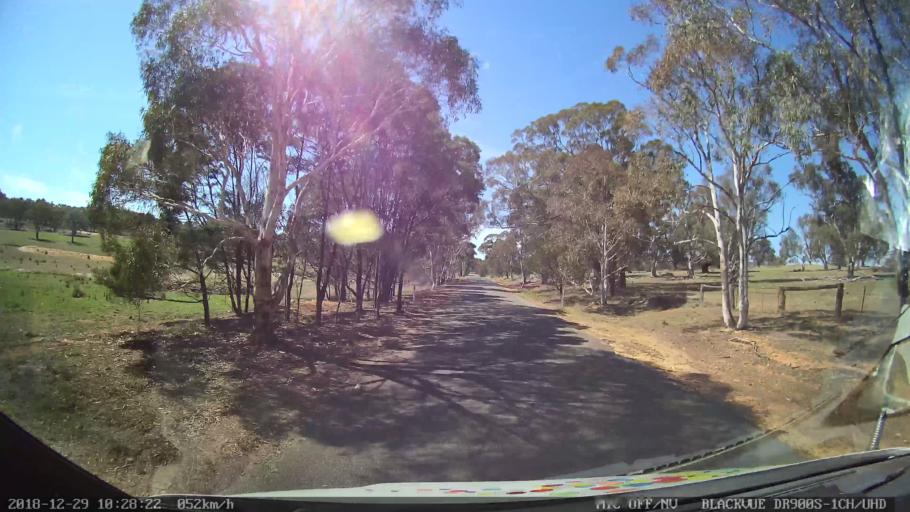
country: AU
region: New South Wales
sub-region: Yass Valley
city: Gundaroo
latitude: -34.9417
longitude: 149.4543
